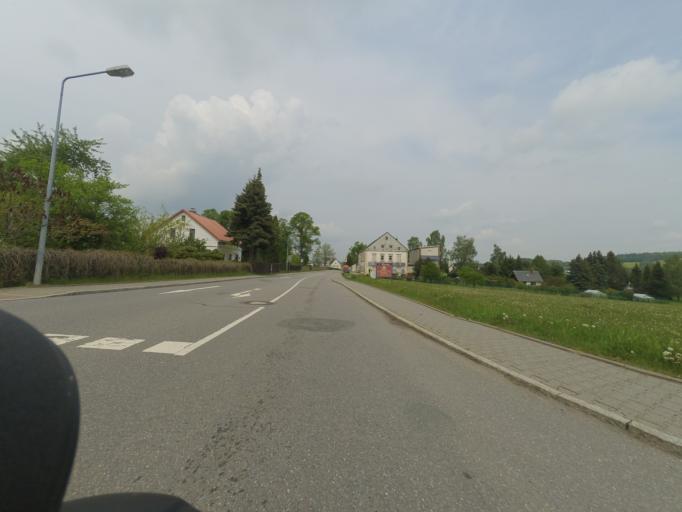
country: DE
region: Saxony
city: Zoblitz
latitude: 50.6547
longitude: 13.2373
